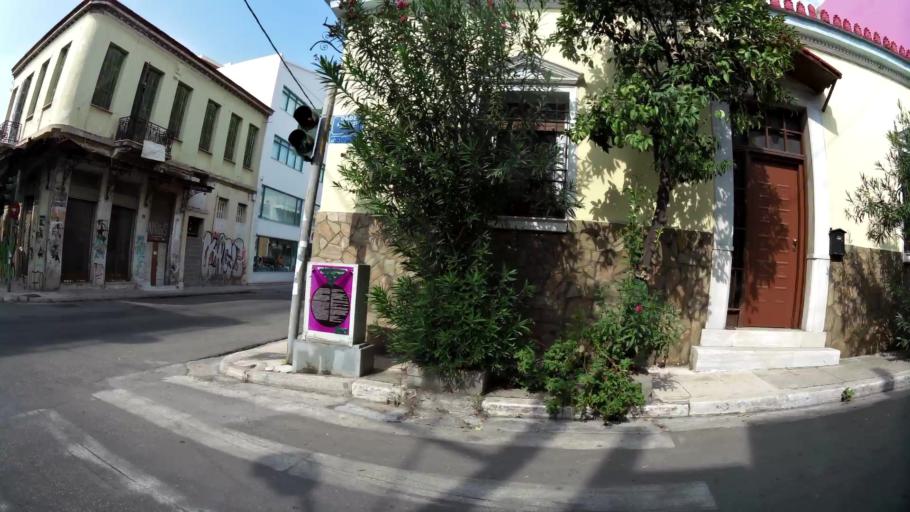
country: GR
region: Attica
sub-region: Nomarchia Athinas
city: Athens
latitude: 37.9945
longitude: 23.7141
